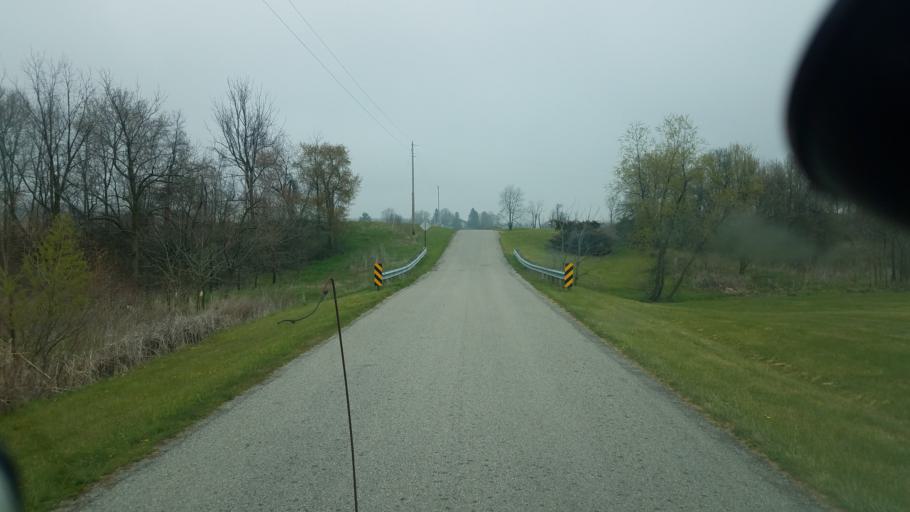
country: US
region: Ohio
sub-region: Logan County
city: Northwood
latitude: 40.5431
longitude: -83.6613
